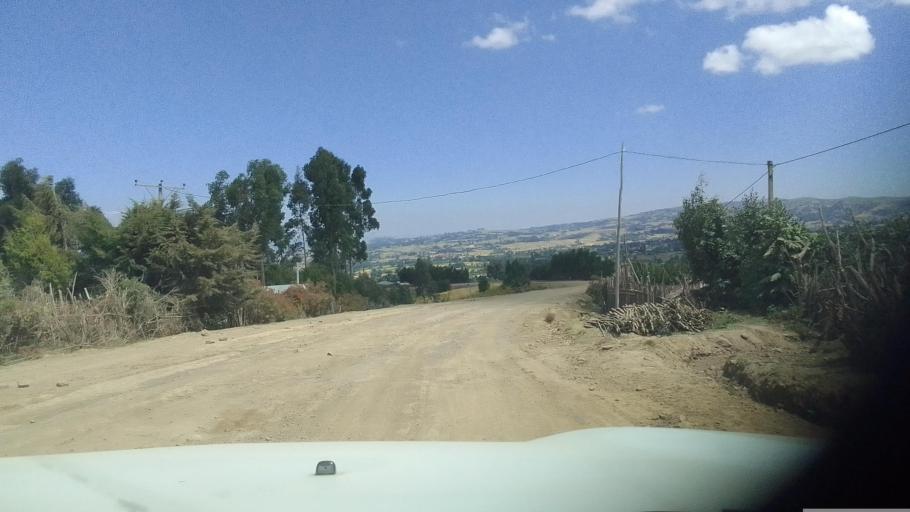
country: ET
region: Oromiya
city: Hagere Hiywet
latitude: 8.8494
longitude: 37.8896
